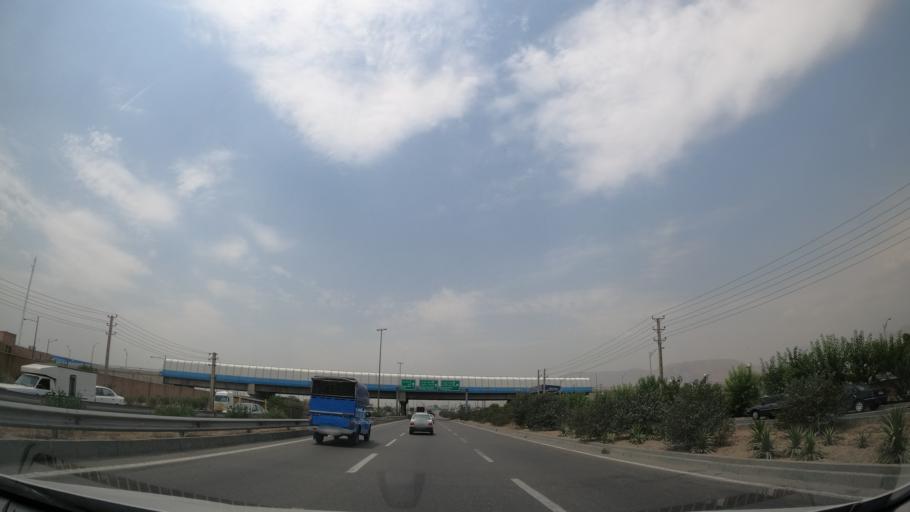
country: IR
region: Tehran
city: Shahr-e Qods
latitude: 35.7006
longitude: 51.1908
